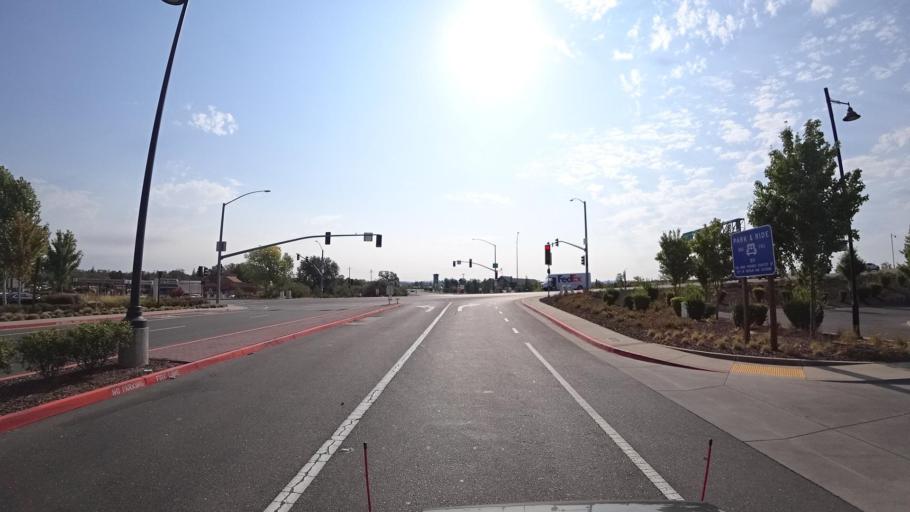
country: US
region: California
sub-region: Placer County
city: Loomis
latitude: 38.8051
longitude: -121.2061
